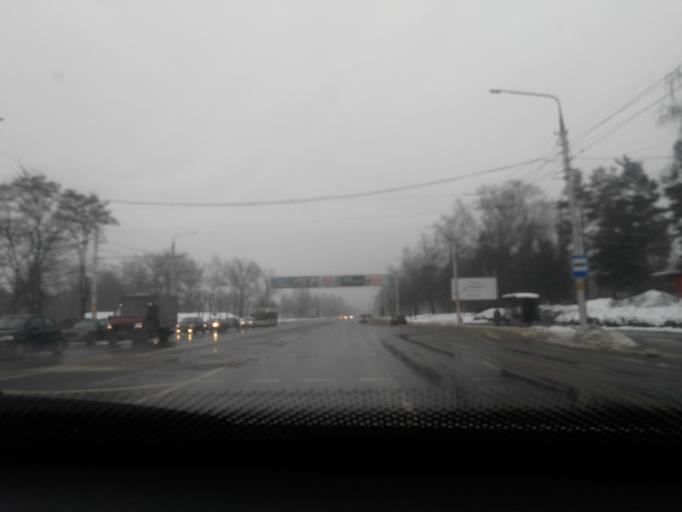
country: BY
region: Mogilev
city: Babruysk
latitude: 53.1777
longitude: 29.1984
